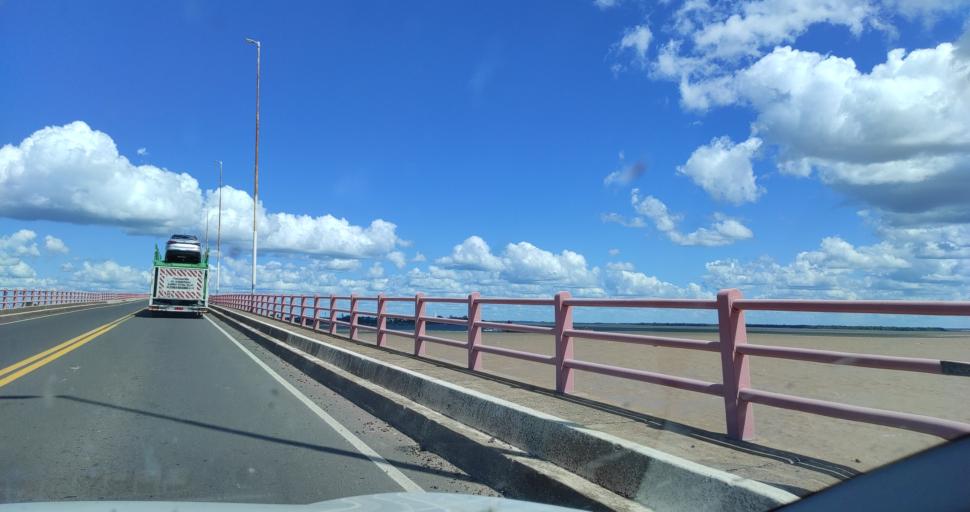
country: AR
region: Corrientes
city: Corrientes
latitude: -27.4640
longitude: -58.8668
